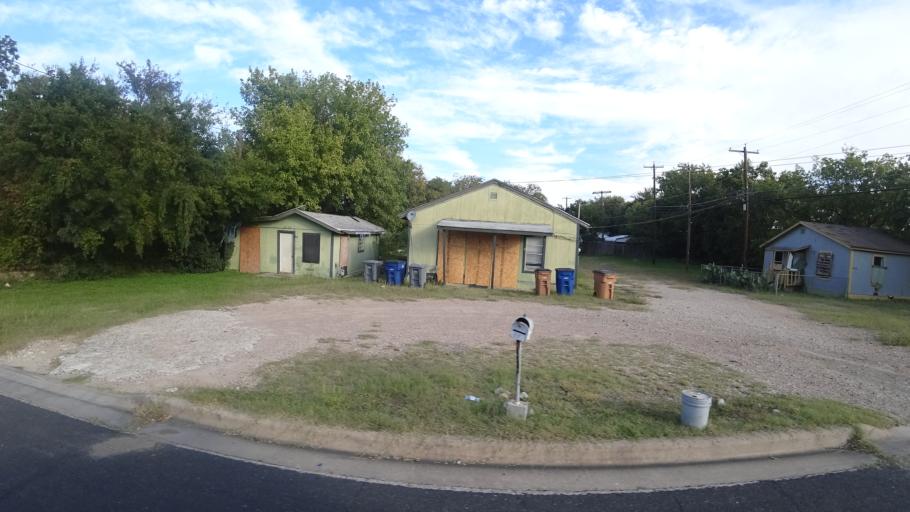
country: US
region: Texas
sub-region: Travis County
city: Austin
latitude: 30.2752
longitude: -97.7044
